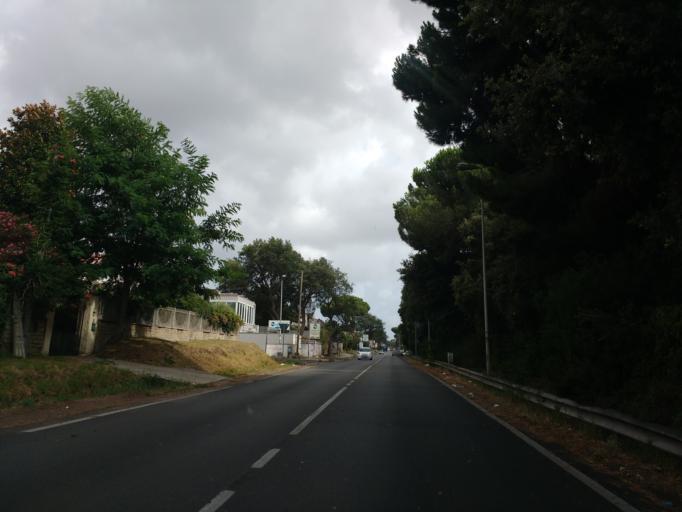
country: IT
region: Latium
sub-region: Citta metropolitana di Roma Capitale
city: Lavinio
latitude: 41.4887
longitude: 12.5980
